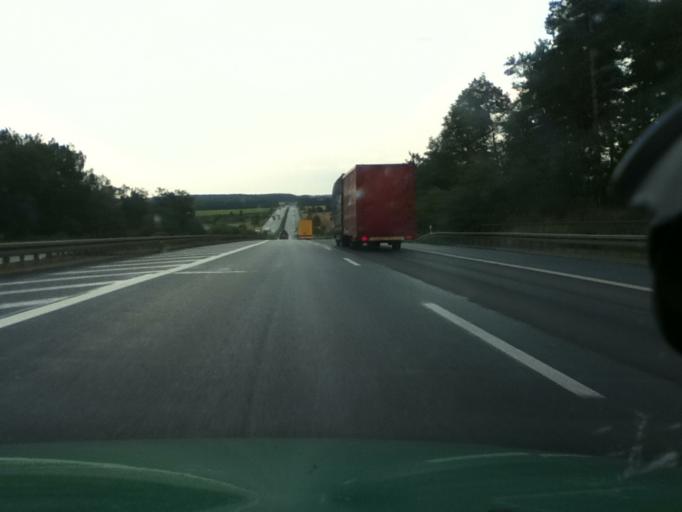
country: DE
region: Saxony
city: Wachau
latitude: 51.1713
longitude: 13.8781
